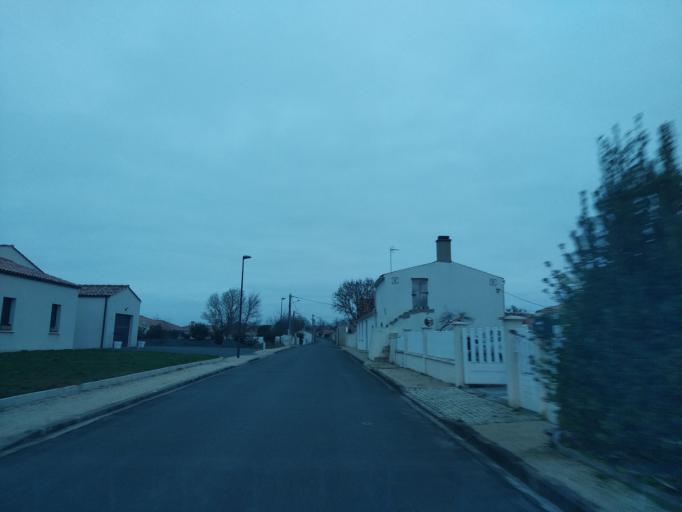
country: FR
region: Pays de la Loire
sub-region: Departement de la Vendee
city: Triaize
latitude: 46.4087
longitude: -1.2641
